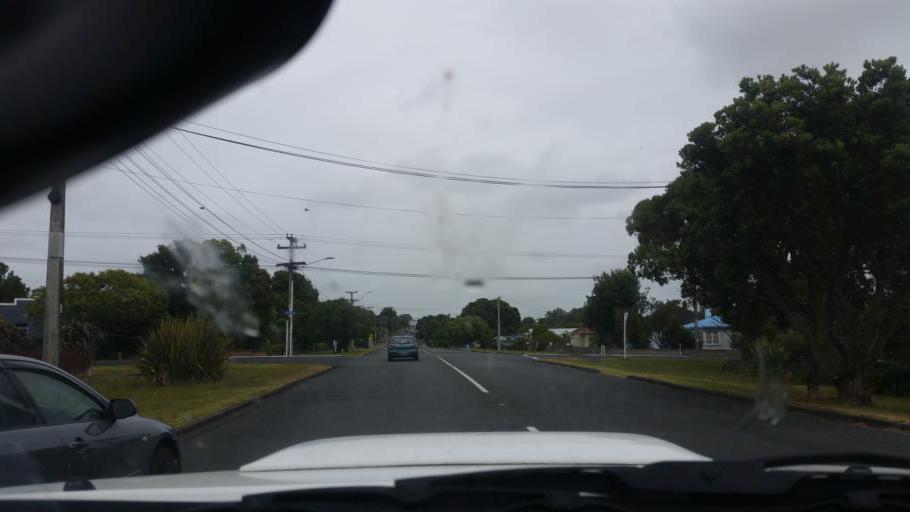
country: NZ
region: Northland
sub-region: Kaipara District
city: Dargaville
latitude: -35.9352
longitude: 173.8734
